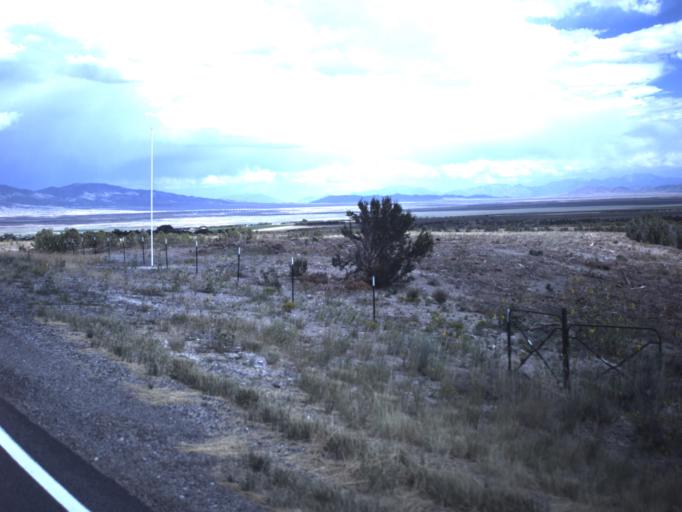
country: US
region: Utah
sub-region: Tooele County
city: Grantsville
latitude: 40.3360
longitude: -112.5071
